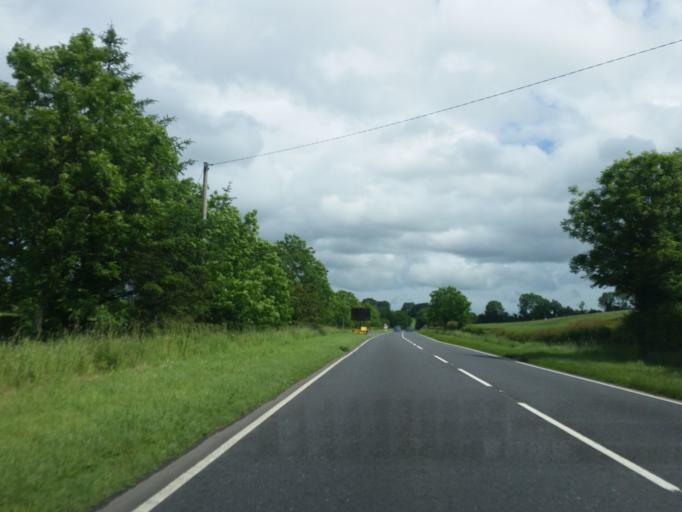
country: IE
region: Ulster
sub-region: County Monaghan
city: Monaghan
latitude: 54.4737
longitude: -7.0622
